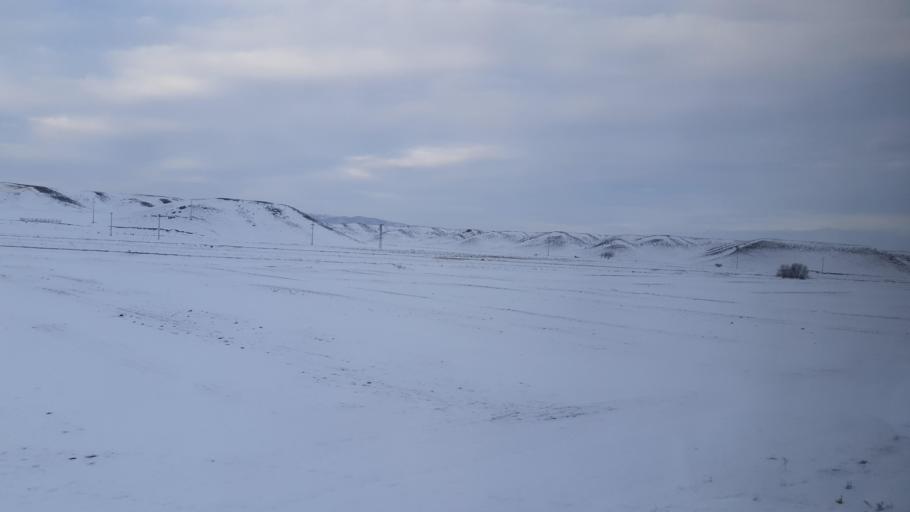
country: TR
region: Kirsehir
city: Mecidiye
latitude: 39.6885
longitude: 34.3897
